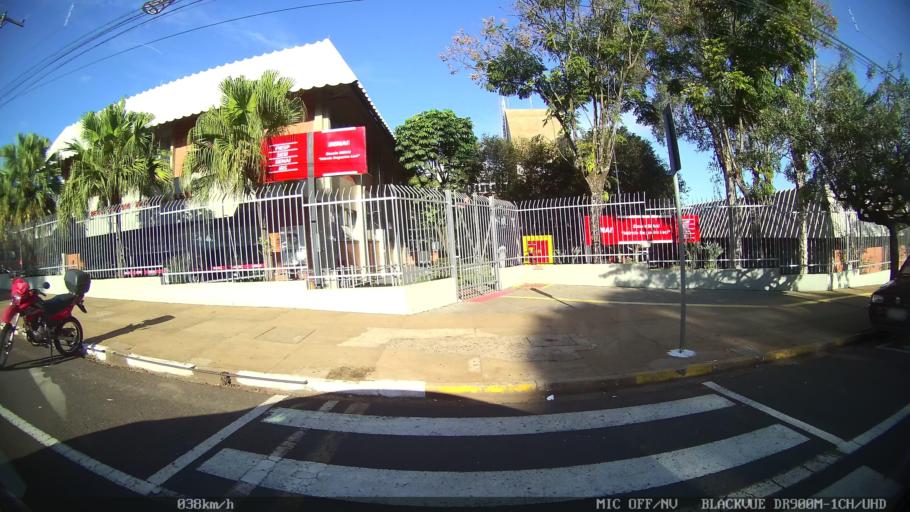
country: BR
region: Sao Paulo
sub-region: Franca
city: Franca
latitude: -20.5174
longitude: -47.3811
